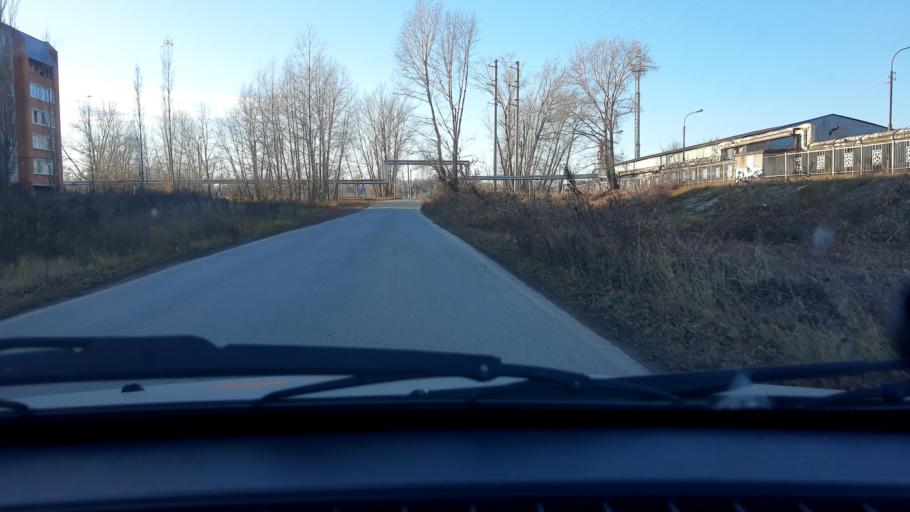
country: RU
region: Bashkortostan
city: Ufa
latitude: 54.6663
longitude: 55.9447
